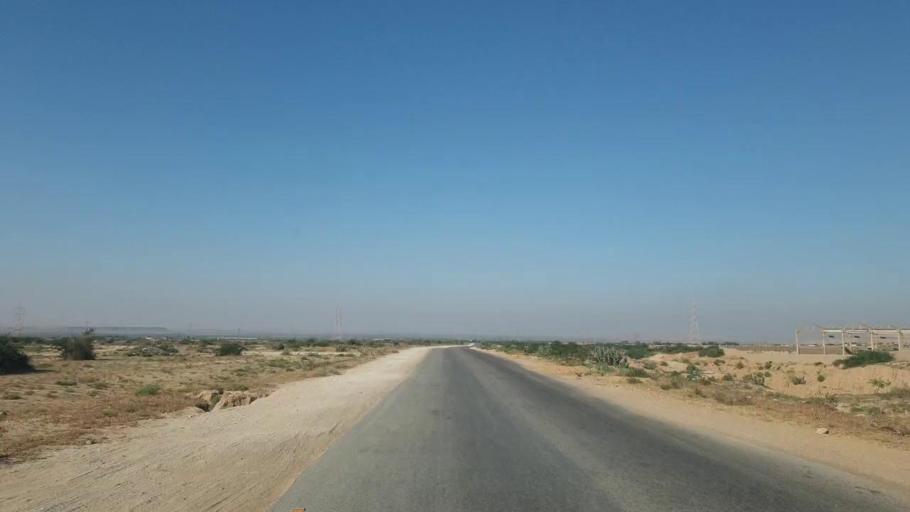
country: PK
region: Sindh
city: Gharo
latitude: 25.1573
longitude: 67.6638
